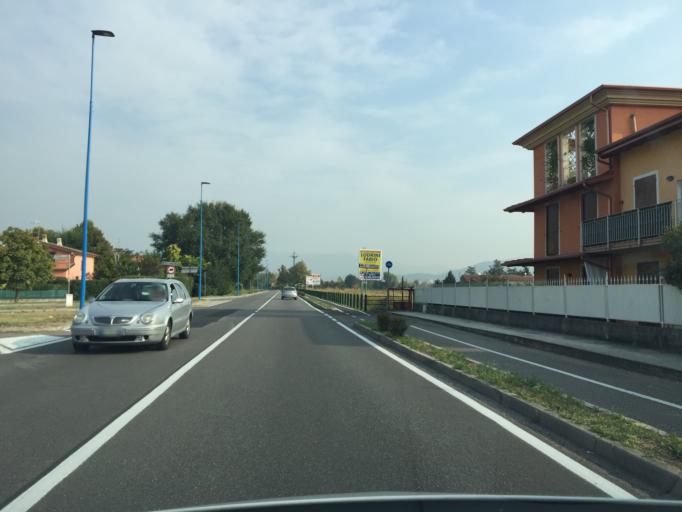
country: IT
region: Lombardy
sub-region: Provincia di Brescia
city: Folzano
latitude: 45.5069
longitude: 10.1914
